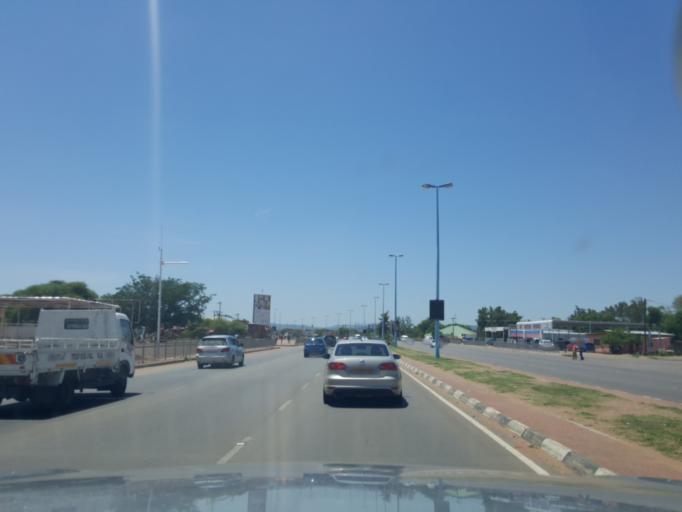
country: BW
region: Kweneng
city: Mogoditshane
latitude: -24.6303
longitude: 25.8728
